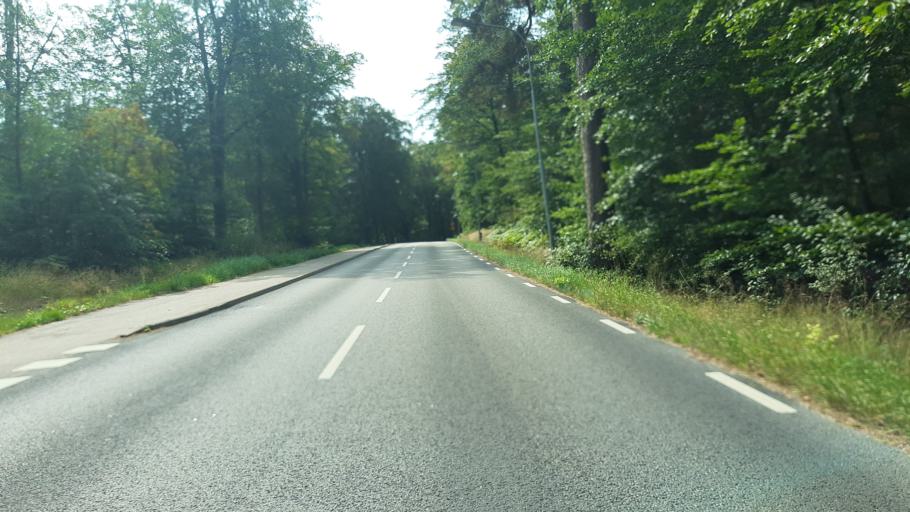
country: SE
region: Blekinge
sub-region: Ronneby Kommun
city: Ronneby
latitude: 56.1748
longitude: 15.2946
